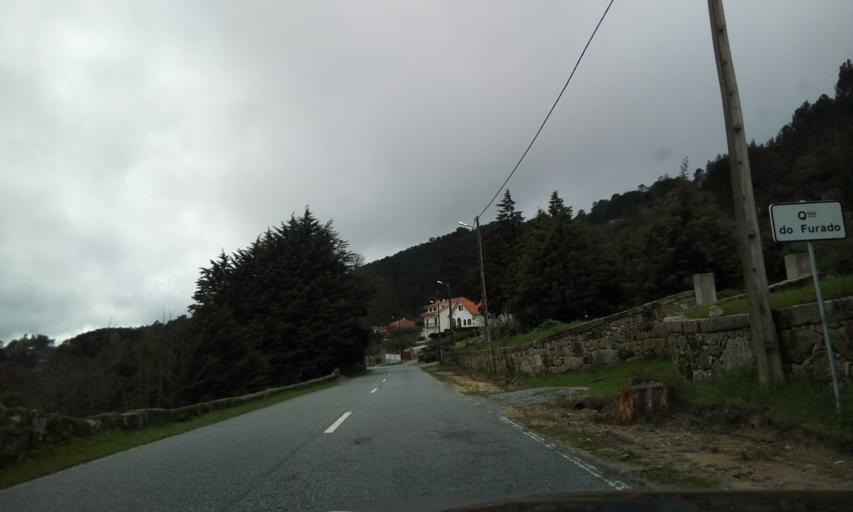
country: PT
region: Guarda
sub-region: Fornos de Algodres
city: Fornos de Algodres
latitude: 40.6151
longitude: -7.5490
